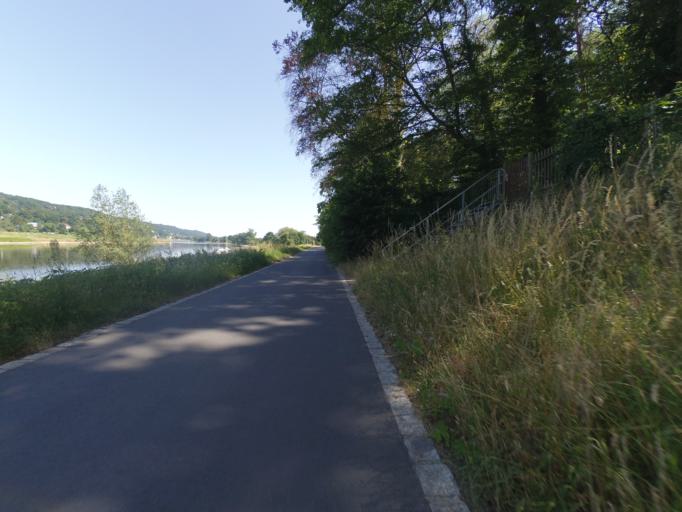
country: DE
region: Saxony
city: Albertstadt
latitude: 51.0416
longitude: 13.8178
